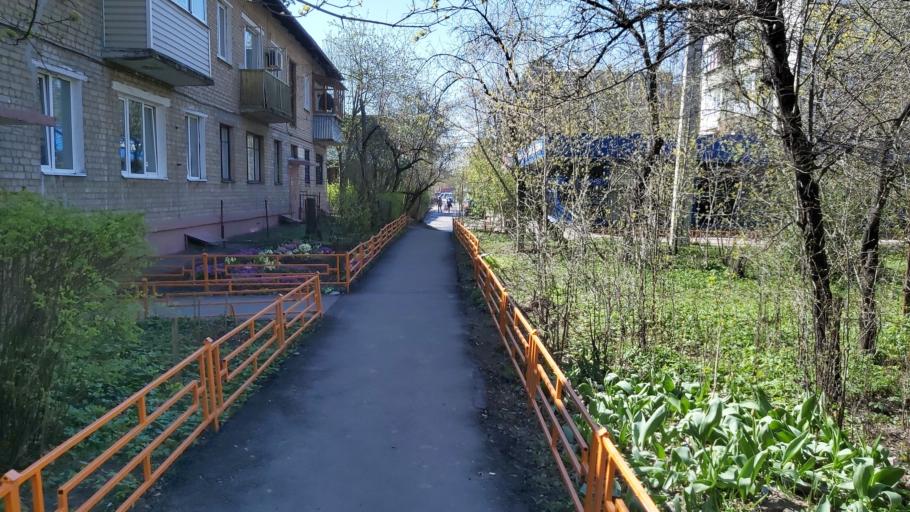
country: RU
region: Moskovskaya
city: Bolshevo
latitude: 55.9261
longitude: 37.8214
